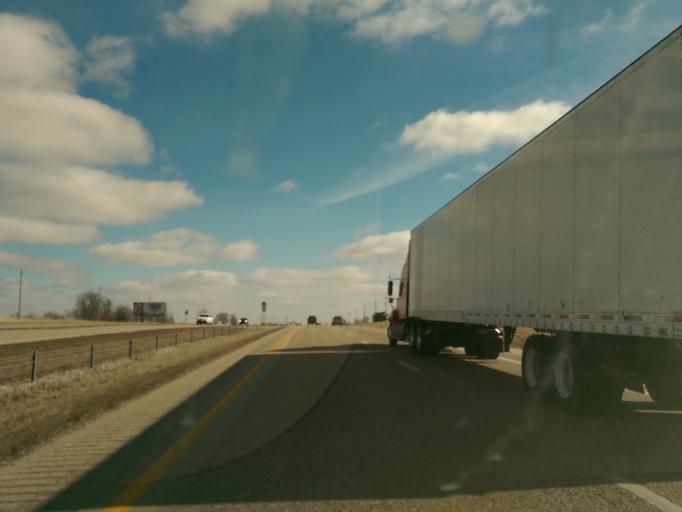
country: US
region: Missouri
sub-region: Montgomery County
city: Montgomery City
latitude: 38.8969
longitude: -91.4468
